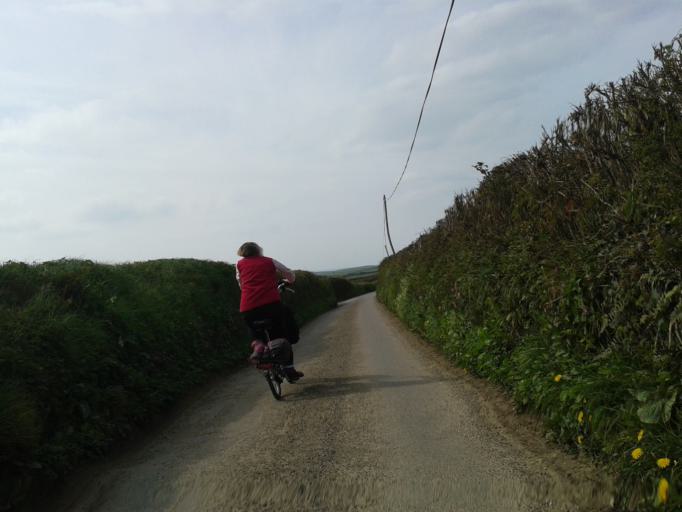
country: GB
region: England
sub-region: Devon
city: Braunton
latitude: 51.1265
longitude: -4.1823
